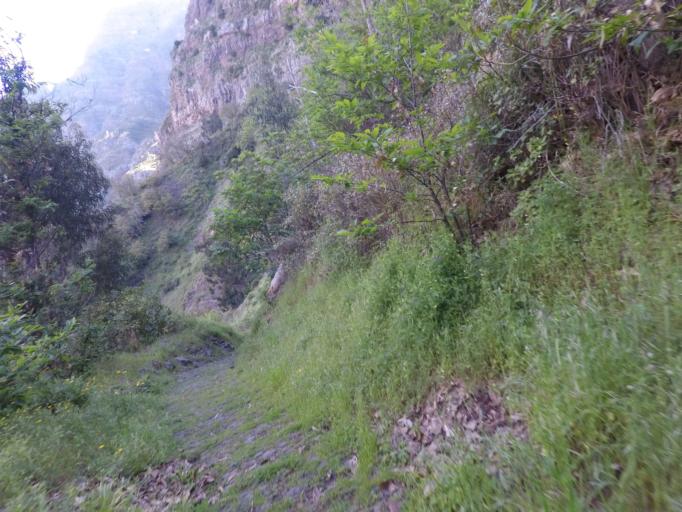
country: PT
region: Madeira
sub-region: Camara de Lobos
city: Curral das Freiras
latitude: 32.7138
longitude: -16.9651
